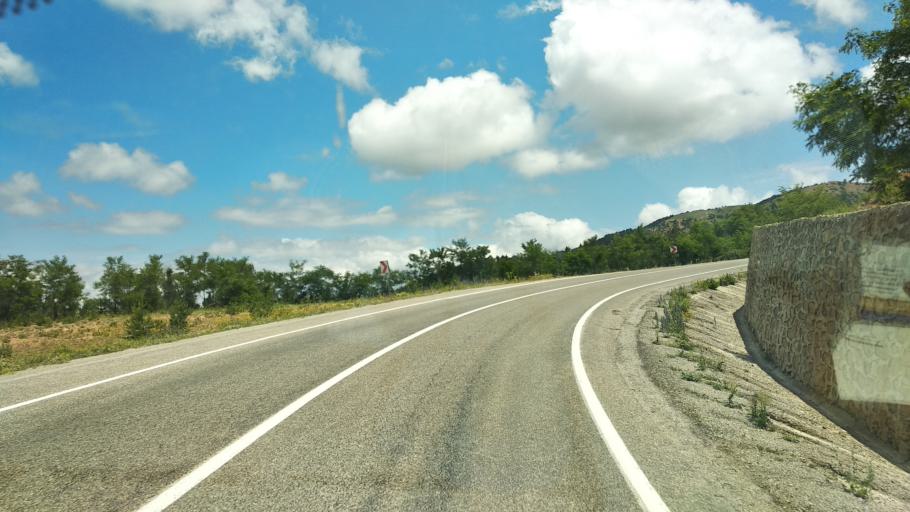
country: TR
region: Gumushane
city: Kose
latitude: 40.2976
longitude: 39.5567
